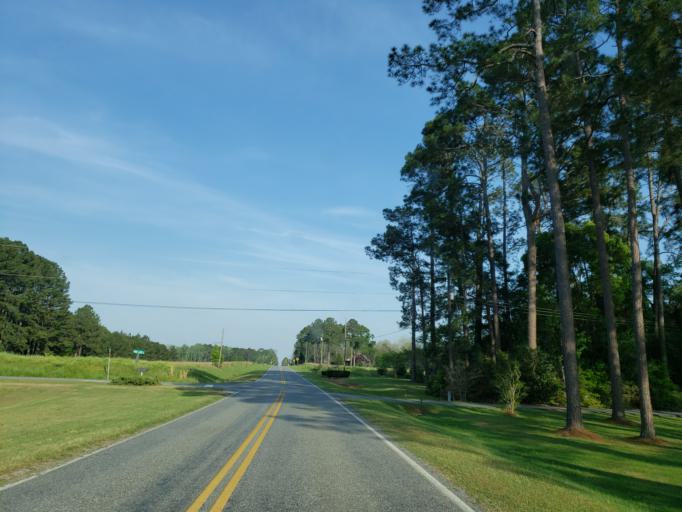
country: US
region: Georgia
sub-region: Tift County
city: Tifton
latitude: 31.4942
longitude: -83.5461
